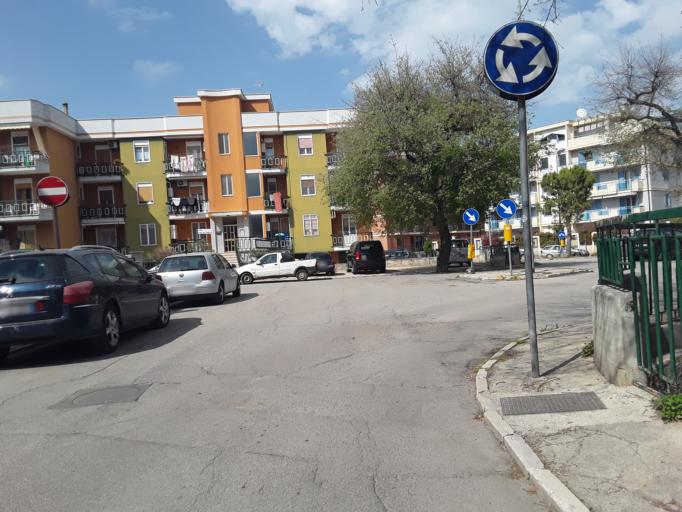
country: IT
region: Apulia
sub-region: Provincia di Bari
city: Ruvo di Puglia
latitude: 41.1219
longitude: 16.4773
